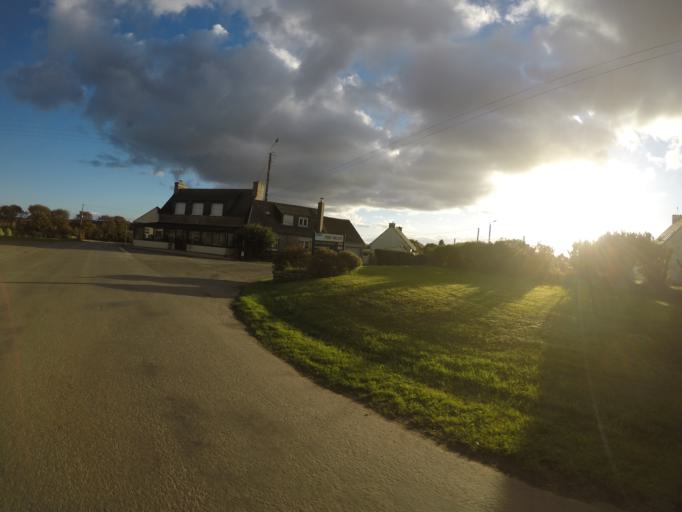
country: FR
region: Brittany
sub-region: Departement des Cotes-d'Armor
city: Louargat
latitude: 48.4641
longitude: -3.3054
